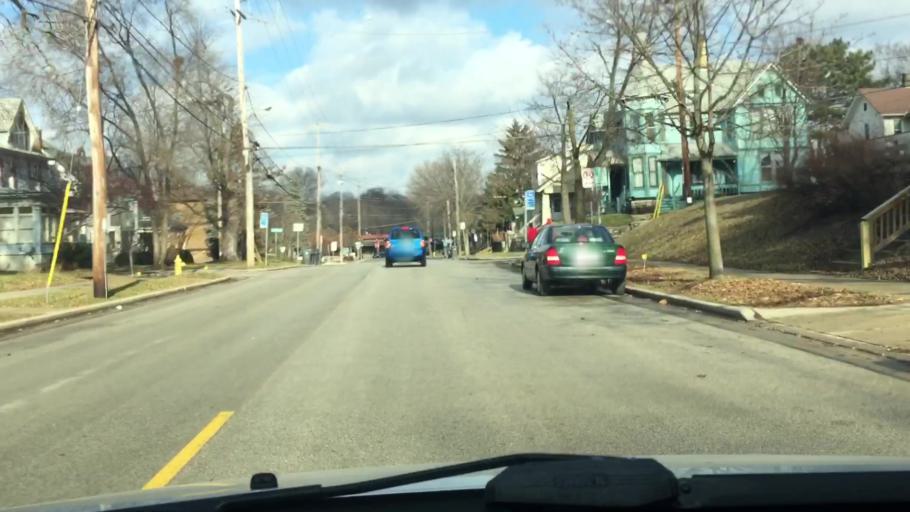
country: US
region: Wisconsin
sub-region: Waukesha County
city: Waukesha
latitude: 43.0084
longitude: -88.2365
